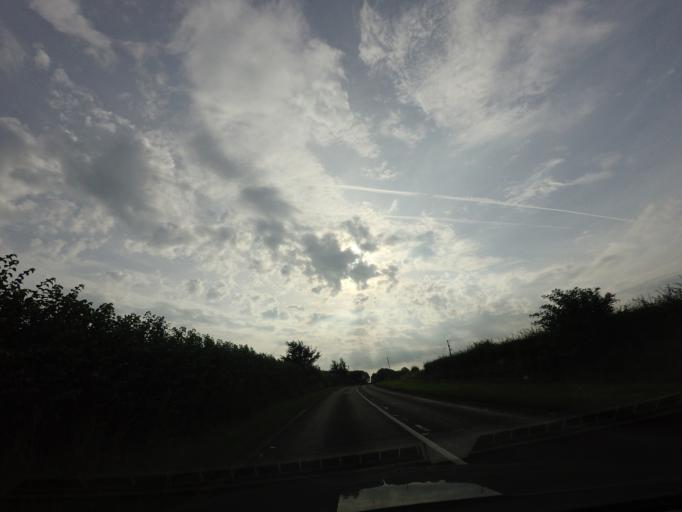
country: GB
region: England
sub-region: Staffordshire
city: Brewood
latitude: 52.6941
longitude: -2.1469
